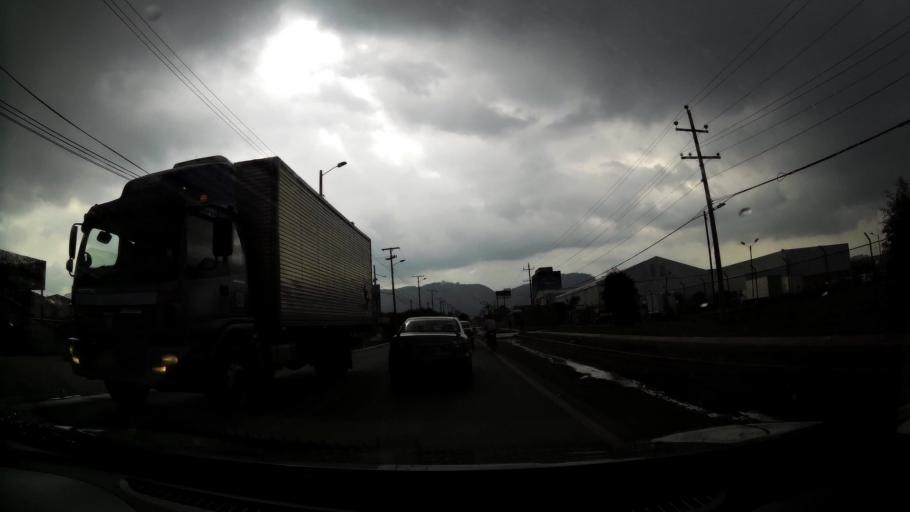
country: CO
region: Cundinamarca
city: Chia
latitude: 4.8493
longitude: -74.0561
